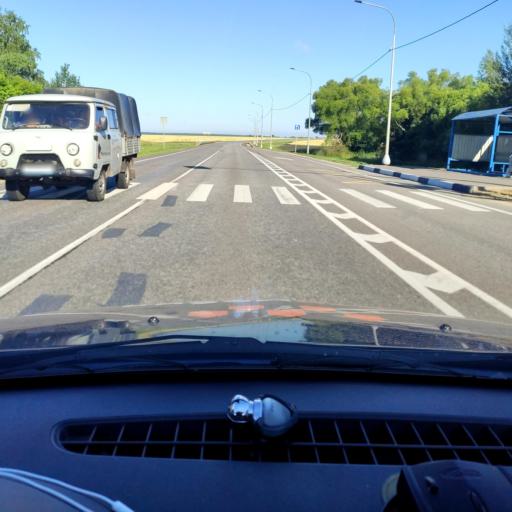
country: RU
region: Orjol
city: Pokrovskoye
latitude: 52.6206
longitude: 36.7341
